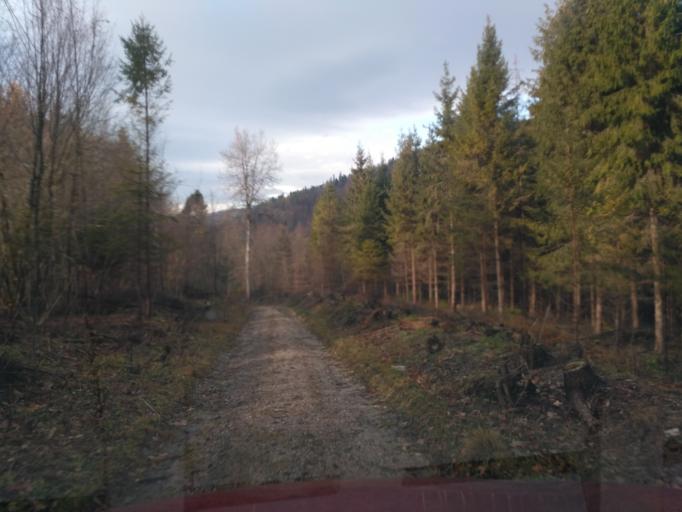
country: SK
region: Kosicky
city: Medzev
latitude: 48.7905
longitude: 20.7584
